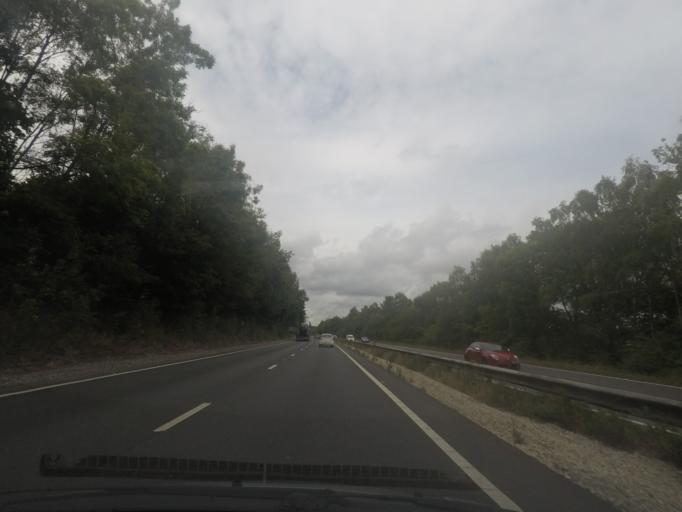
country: GB
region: England
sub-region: Hampshire
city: Overton
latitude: 51.2640
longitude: -1.3392
